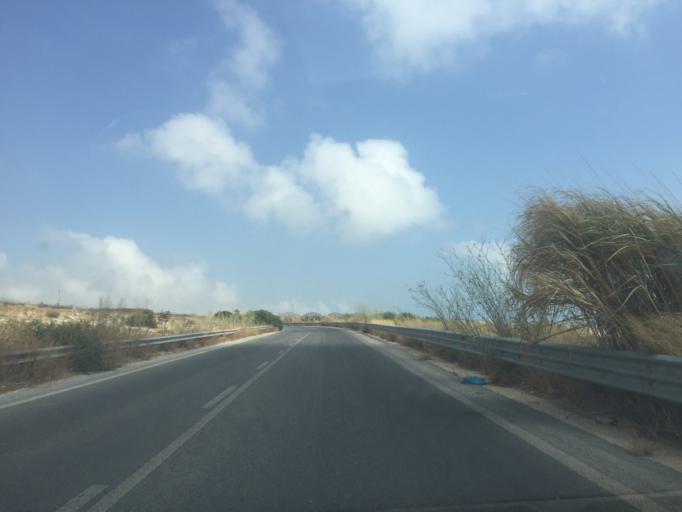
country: IT
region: Sicily
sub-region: Ragusa
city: Donnalucata
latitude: 36.7740
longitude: 14.6187
